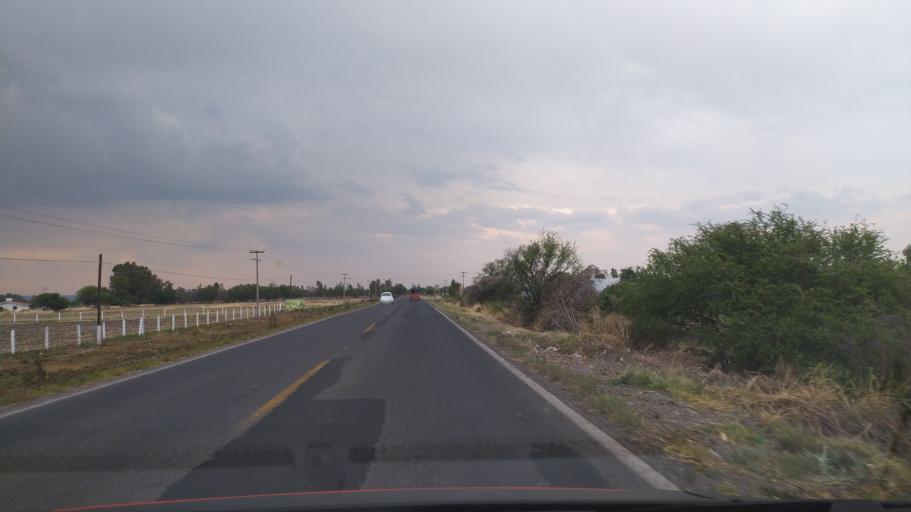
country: MX
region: Guanajuato
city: Ciudad Manuel Doblado
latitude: 20.7797
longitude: -101.9100
